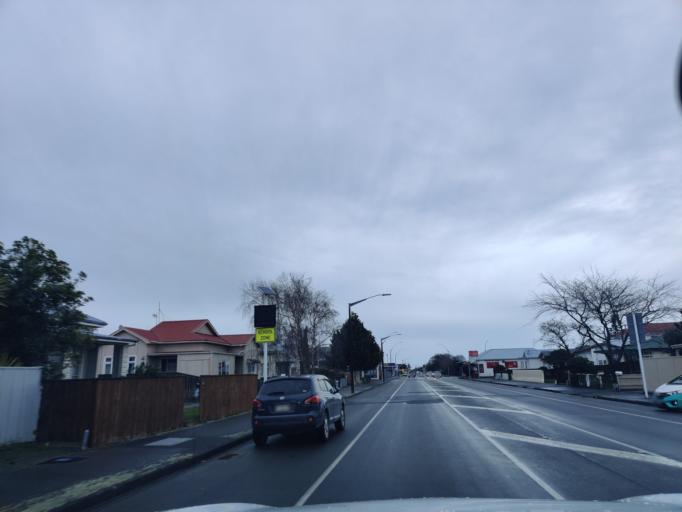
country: NZ
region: Manawatu-Wanganui
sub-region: Palmerston North City
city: Palmerston North
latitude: -40.3473
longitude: 175.6120
